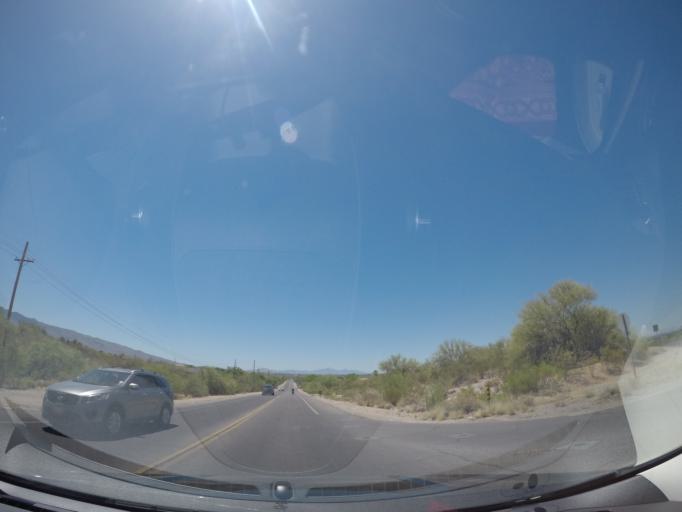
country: US
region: Arizona
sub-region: Pima County
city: Tanque Verde
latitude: 32.2782
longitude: -110.7726
